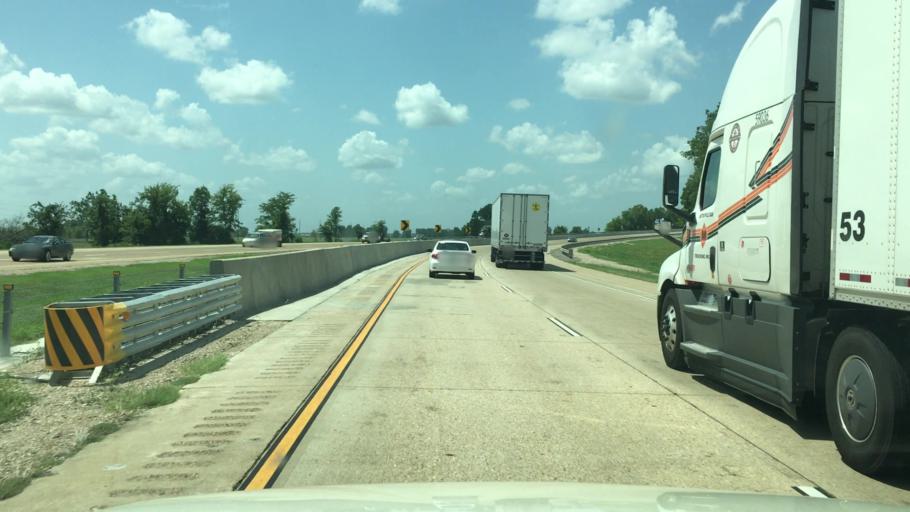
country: US
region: Arkansas
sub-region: Miller County
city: Texarkana
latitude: 33.5527
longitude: -93.8673
